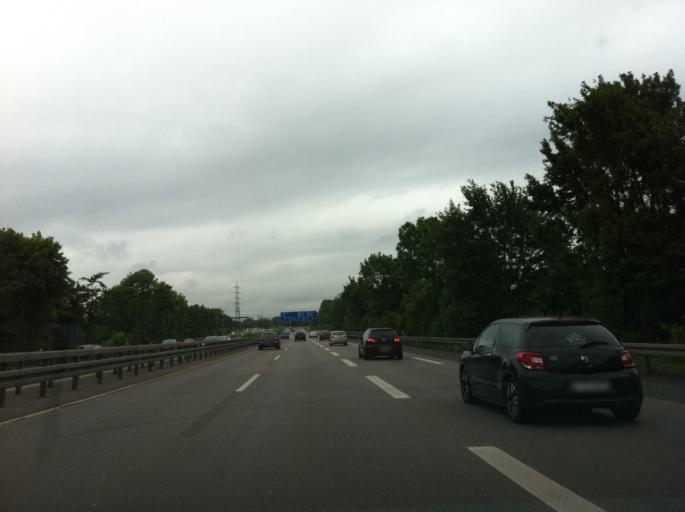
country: DE
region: Hesse
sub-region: Regierungsbezirk Darmstadt
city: Eschborn
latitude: 50.1327
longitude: 8.6018
